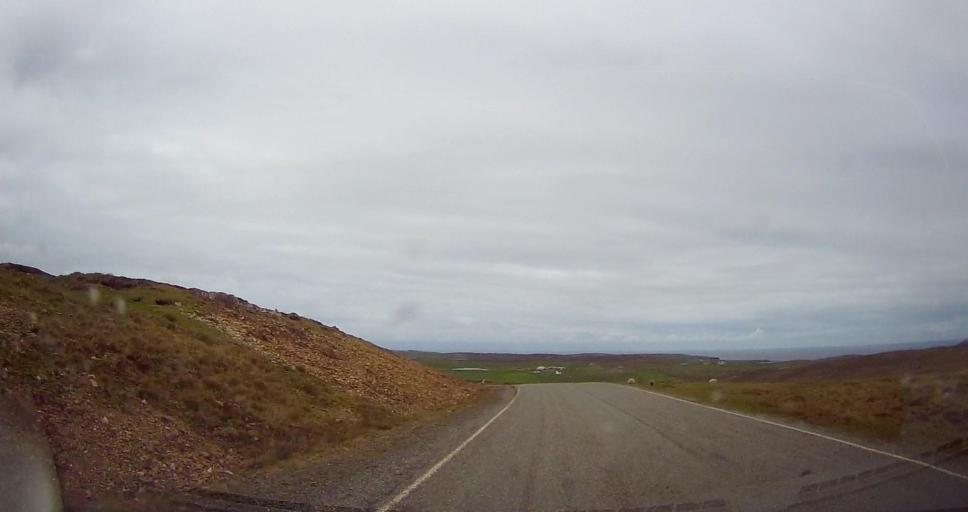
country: GB
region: Scotland
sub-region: Shetland Islands
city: Lerwick
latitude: 60.4875
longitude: -1.5281
